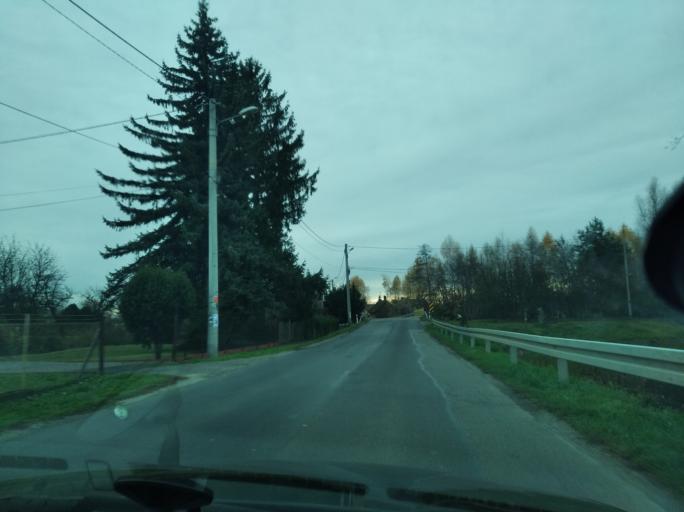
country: PL
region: Subcarpathian Voivodeship
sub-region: Powiat lancucki
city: Czarna
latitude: 50.0898
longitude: 22.1849
